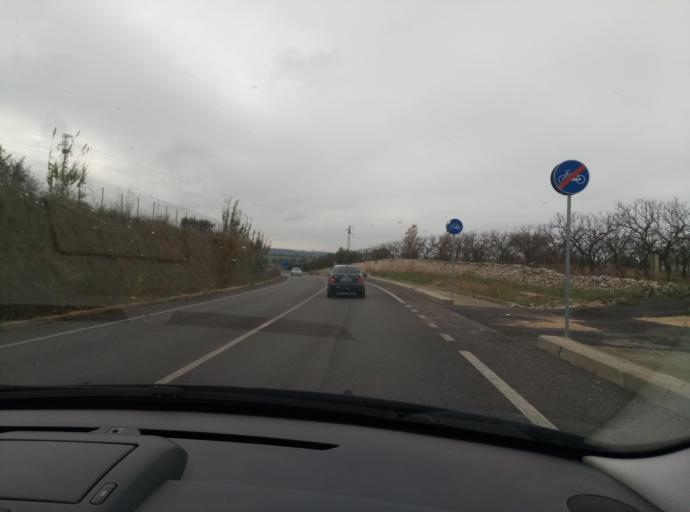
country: IT
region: Apulia
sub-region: Provincia di Bari
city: Acquaviva delle Fonti
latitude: 40.8860
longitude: 16.8154
